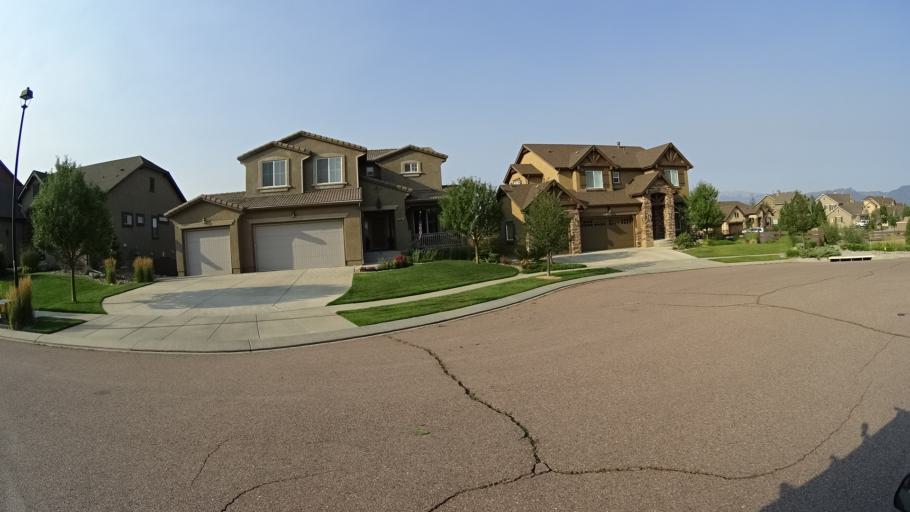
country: US
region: Colorado
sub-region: El Paso County
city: Black Forest
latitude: 38.9759
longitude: -104.7332
